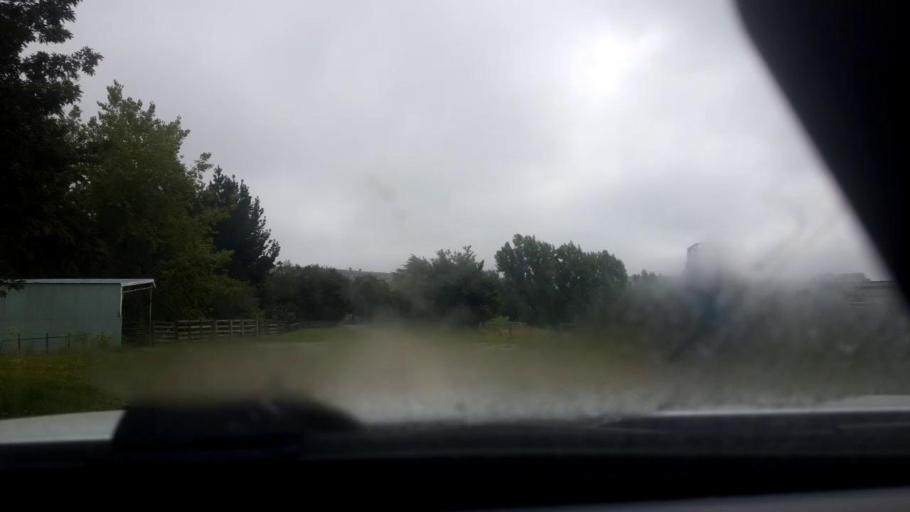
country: NZ
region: Canterbury
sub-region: Timaru District
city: Pleasant Point
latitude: -44.1908
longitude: 171.0799
